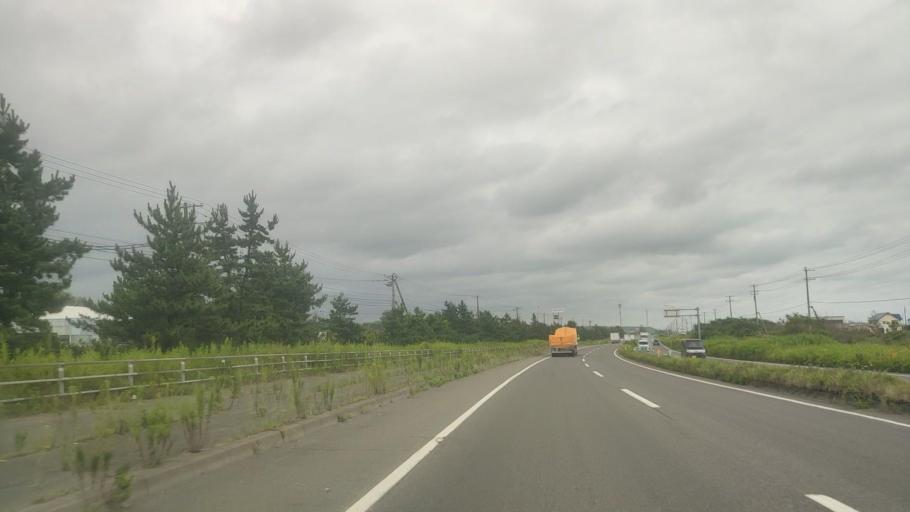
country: JP
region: Hokkaido
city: Shiraoi
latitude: 42.5314
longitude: 141.3244
